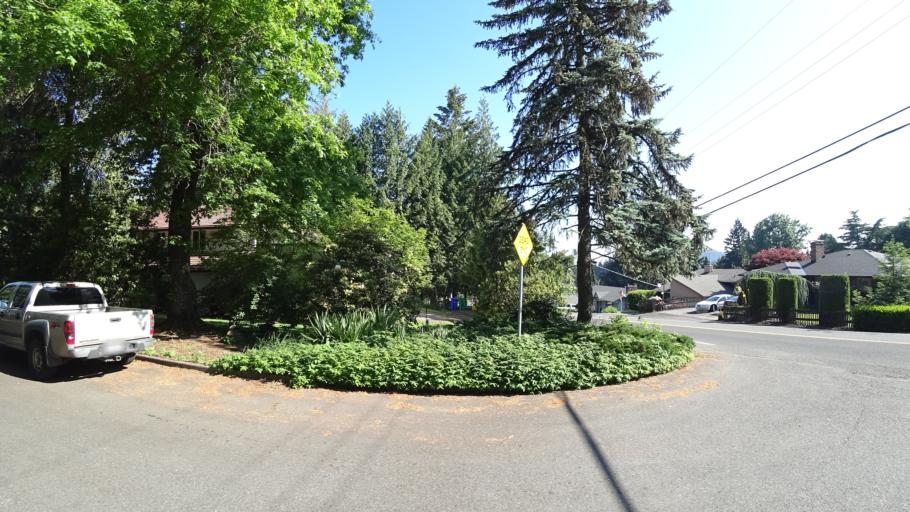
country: US
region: Oregon
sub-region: Clackamas County
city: Happy Valley
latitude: 45.4703
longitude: -122.5365
